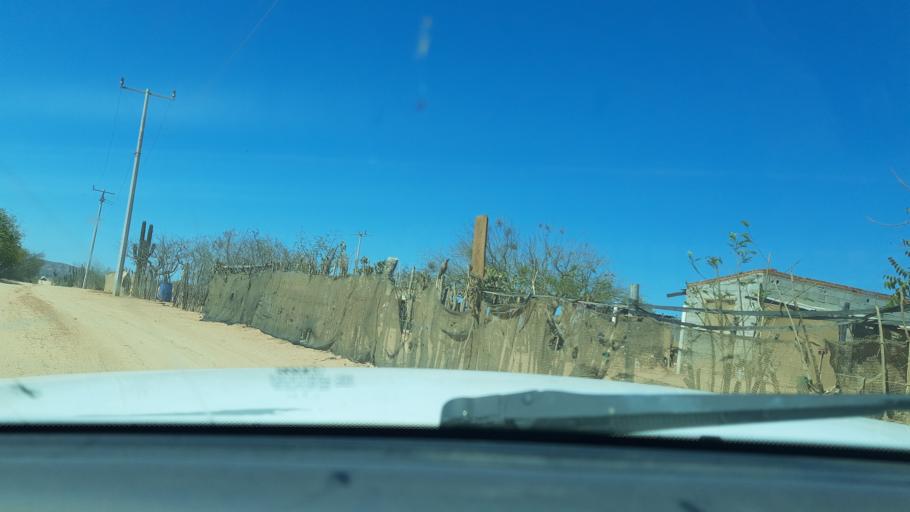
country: MX
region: Baja California Sur
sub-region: La Paz
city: Meliton Albanez Dominguez
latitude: 23.6456
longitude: -110.2624
